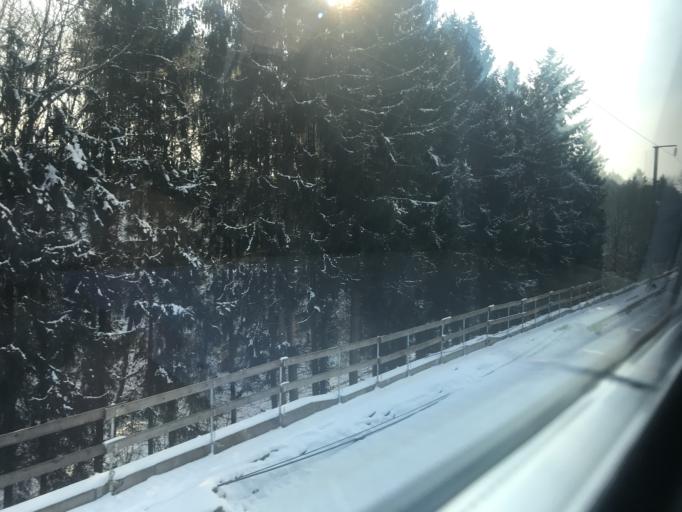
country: LU
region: Luxembourg
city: Kirchberg
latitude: 49.6133
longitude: 6.1615
